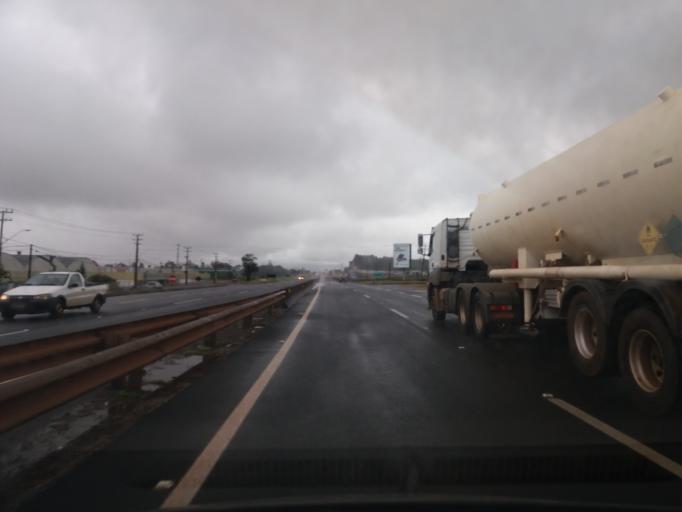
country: BR
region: Parana
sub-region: Cascavel
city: Cascavel
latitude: -24.9941
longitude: -53.5129
